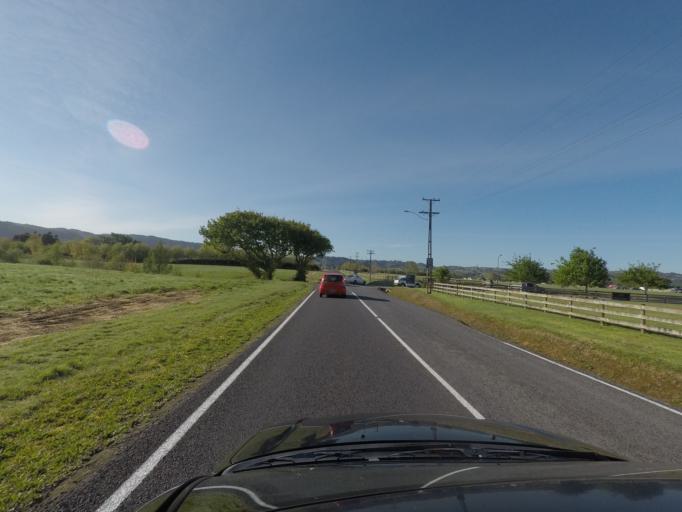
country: NZ
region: Auckland
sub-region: Auckland
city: Red Hill
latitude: -37.0036
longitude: 175.0434
